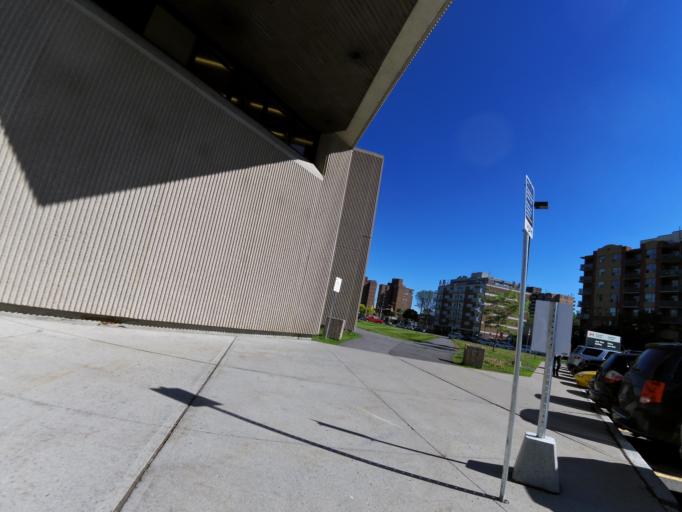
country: CA
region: Ontario
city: Ottawa
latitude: 45.4070
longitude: -75.7336
